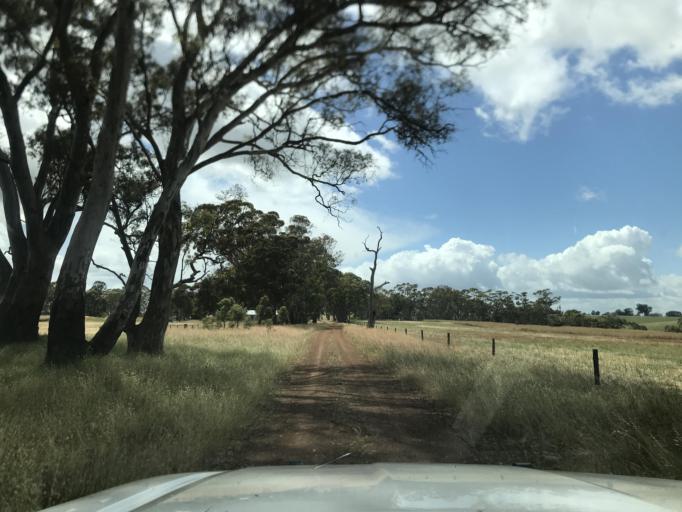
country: AU
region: South Australia
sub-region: Wattle Range
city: Penola
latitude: -37.1852
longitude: 141.4809
